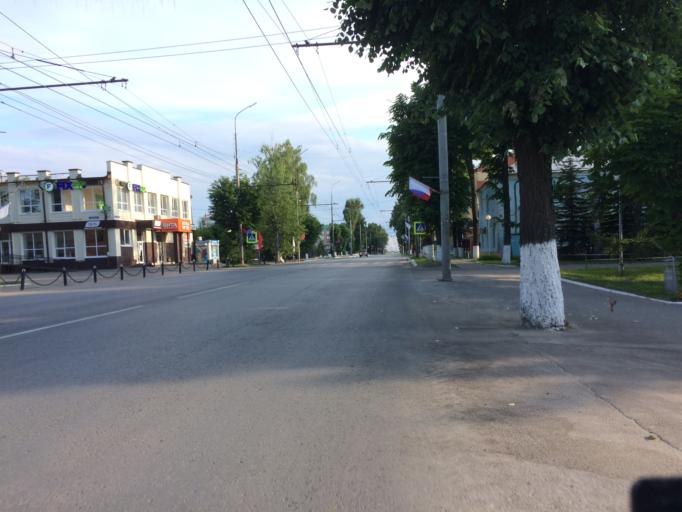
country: RU
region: Mariy-El
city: Medvedevo
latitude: 56.6333
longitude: 47.8038
